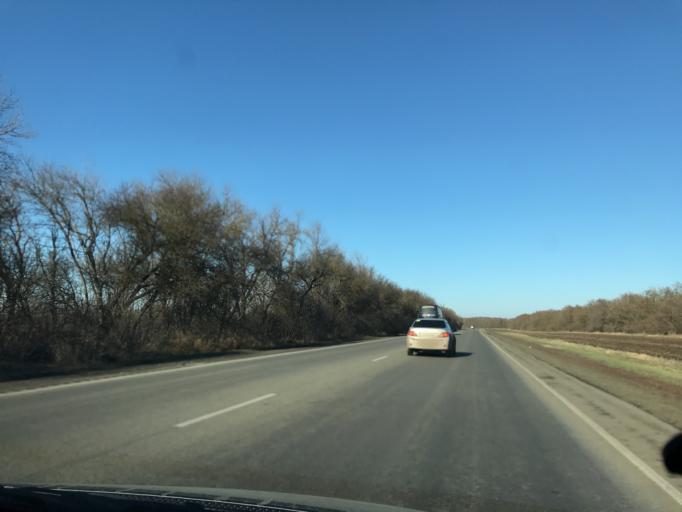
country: RU
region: Rostov
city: Kirovskaya
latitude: 46.9529
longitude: 40.0797
